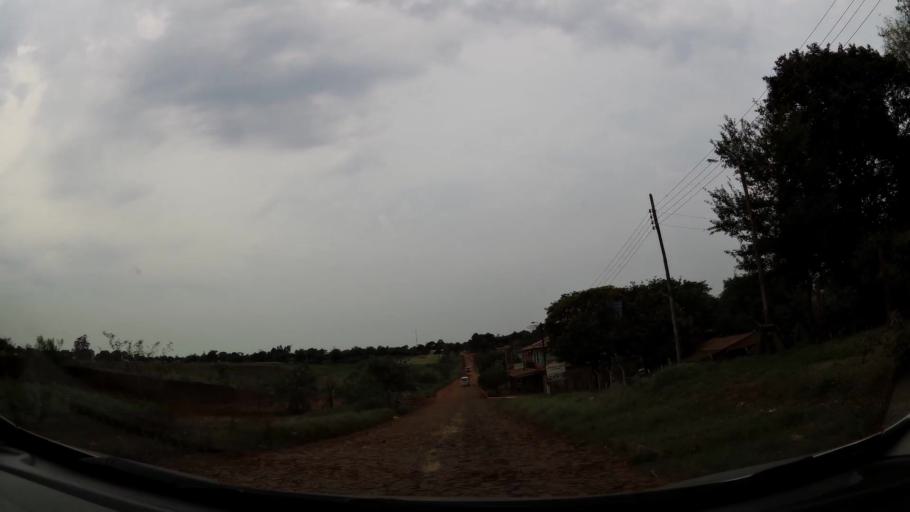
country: PY
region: Alto Parana
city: Presidente Franco
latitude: -25.5429
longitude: -54.6523
